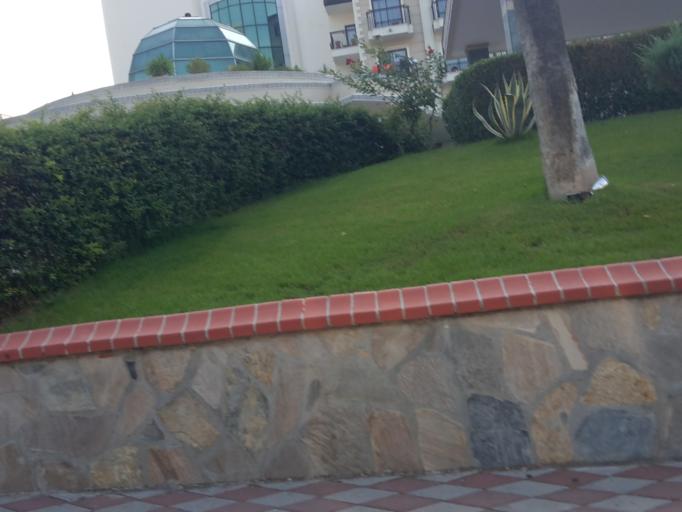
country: TR
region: Antalya
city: Kemer
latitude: 36.6142
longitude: 30.5564
